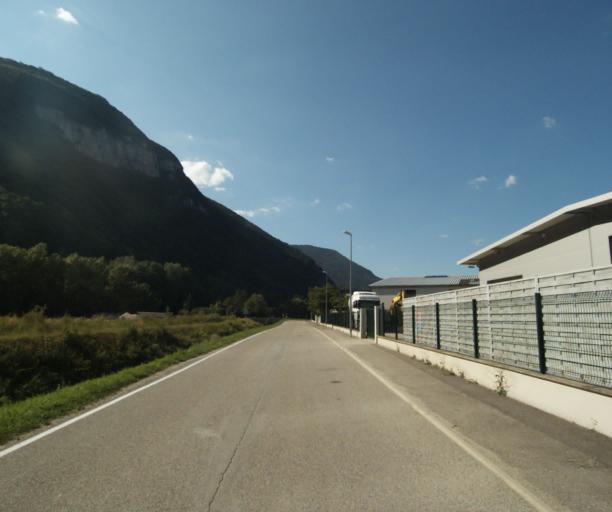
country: FR
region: Rhone-Alpes
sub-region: Departement de l'Isere
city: Noyarey
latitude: 45.2528
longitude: 5.6252
